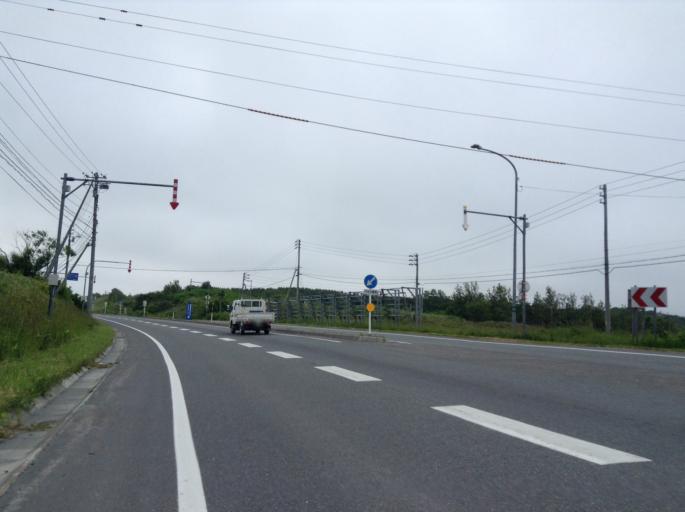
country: JP
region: Hokkaido
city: Wakkanai
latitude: 45.3757
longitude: 141.7127
